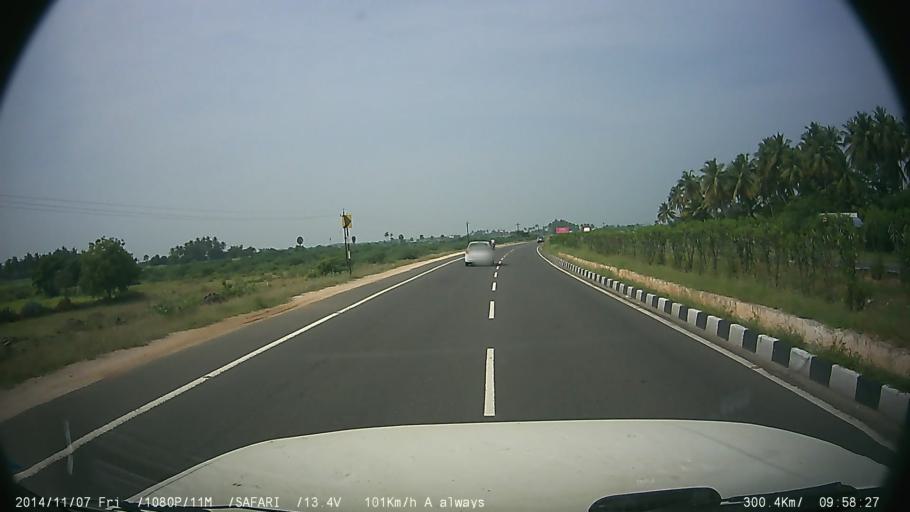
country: IN
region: Tamil Nadu
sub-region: Tiruppur
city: Uttukkuli
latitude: 11.2190
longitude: 77.4535
